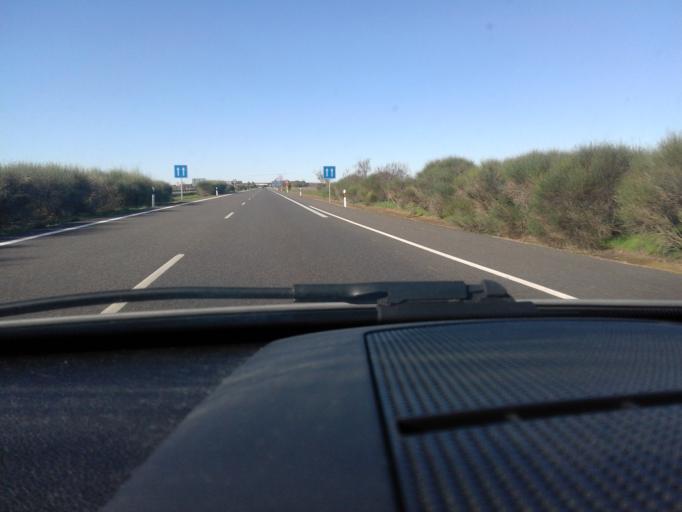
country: ES
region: Castille and Leon
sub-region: Provincia de Leon
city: Calzada del Coto
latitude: 42.3846
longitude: -5.0843
